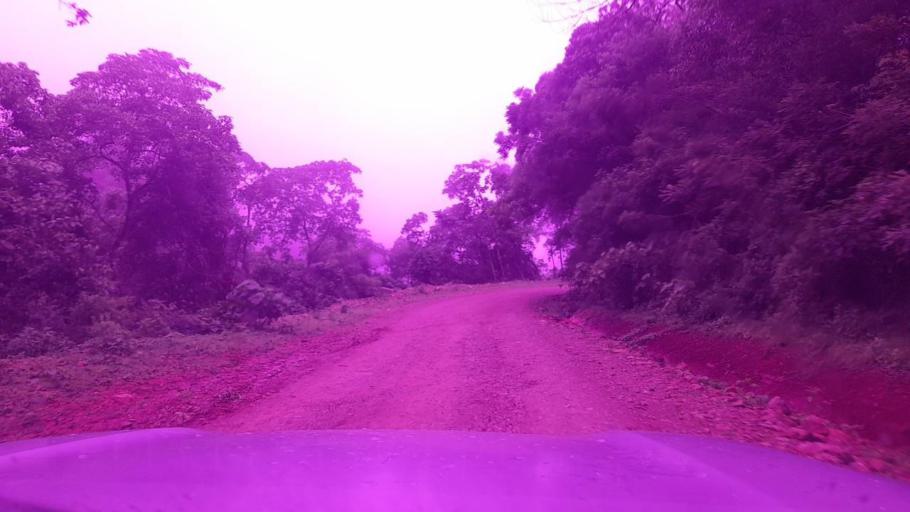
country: ET
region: Southern Nations, Nationalities, and People's Region
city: Bonga
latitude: 7.5178
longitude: 36.0584
